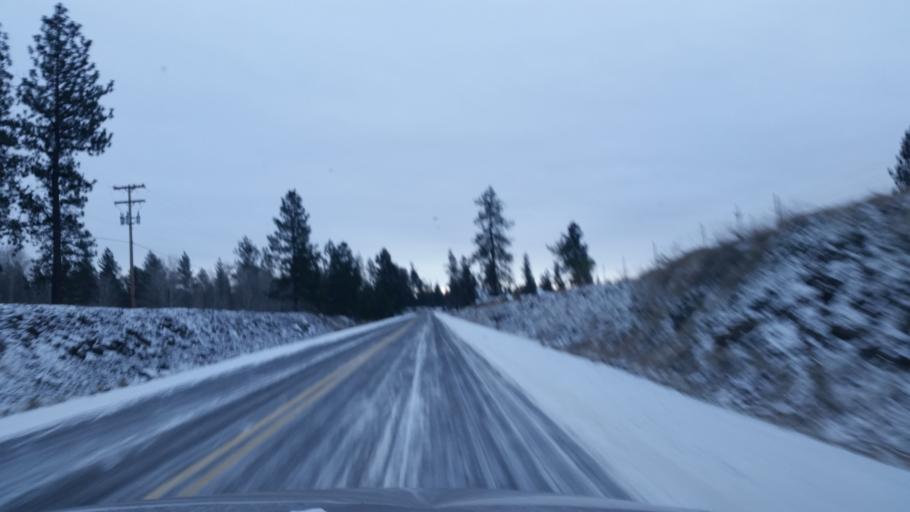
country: US
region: Washington
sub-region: Spokane County
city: Cheney
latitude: 47.4717
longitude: -117.5434
